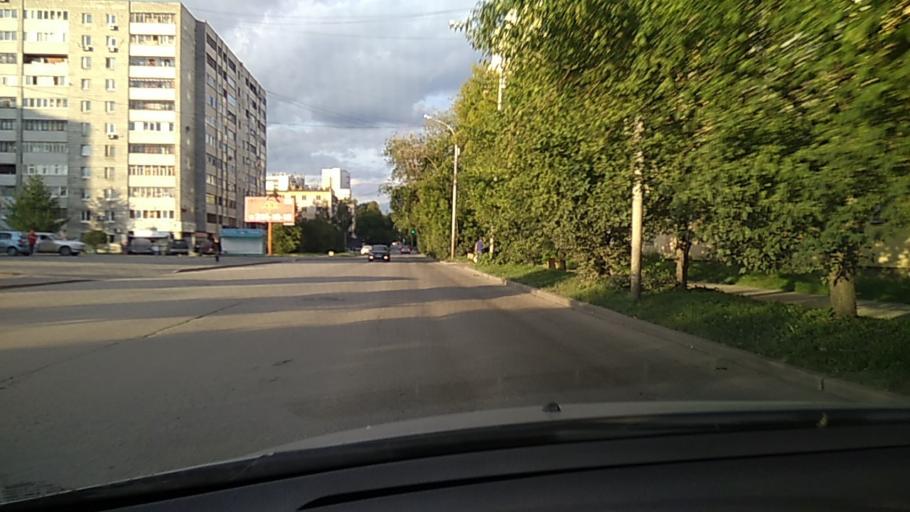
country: RU
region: Sverdlovsk
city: Yekaterinburg
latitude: 56.8938
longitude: 60.6185
